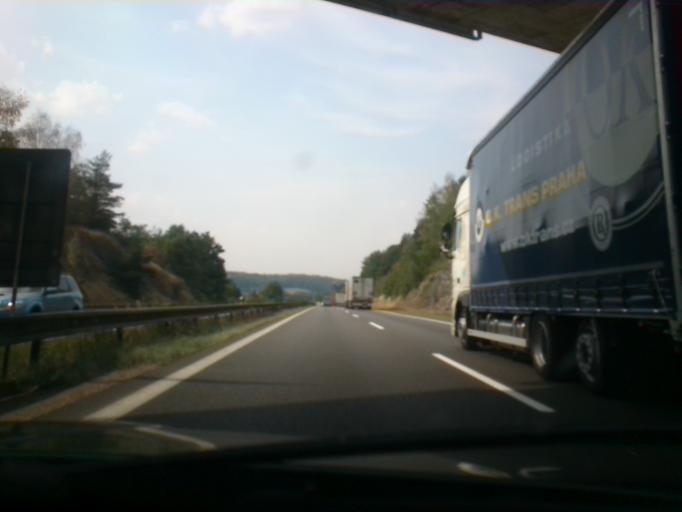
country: CZ
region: Central Bohemia
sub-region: Okres Praha-Vychod
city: Mnichovice
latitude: 49.9033
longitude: 14.7369
